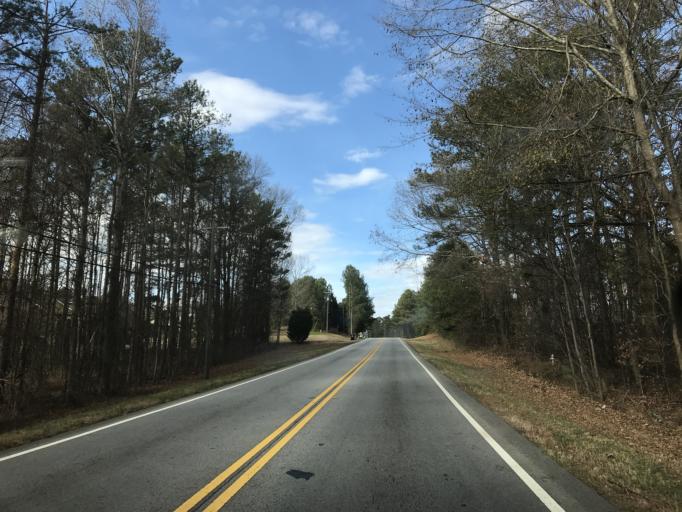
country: US
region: Georgia
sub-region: Douglas County
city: Douglasville
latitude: 33.7865
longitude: -84.7971
